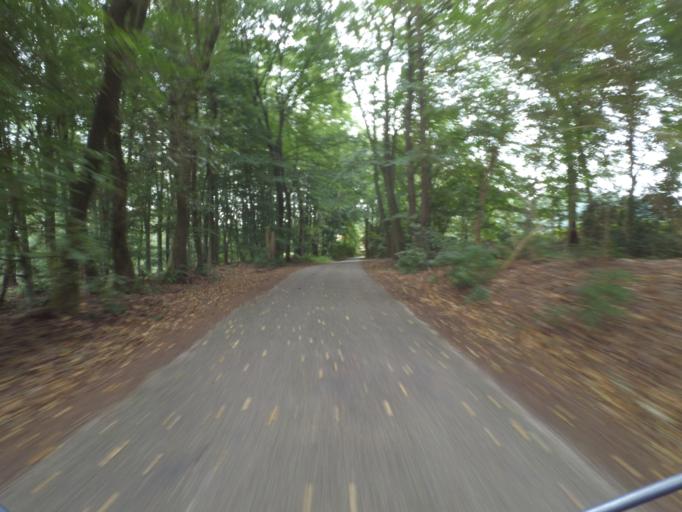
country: NL
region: Overijssel
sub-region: Gemeente Oldenzaal
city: Oldenzaal
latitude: 52.3234
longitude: 6.9564
